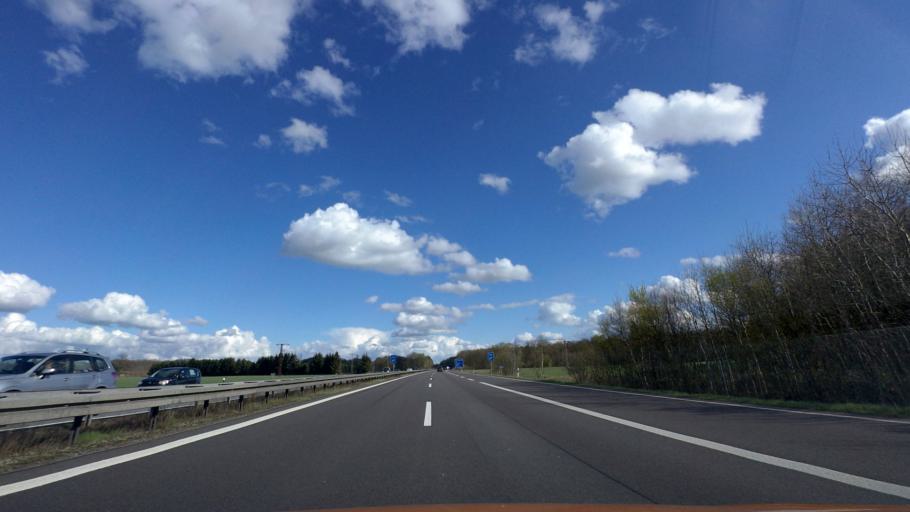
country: DE
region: Brandenburg
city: Putlitz
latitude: 53.2842
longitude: 12.0750
